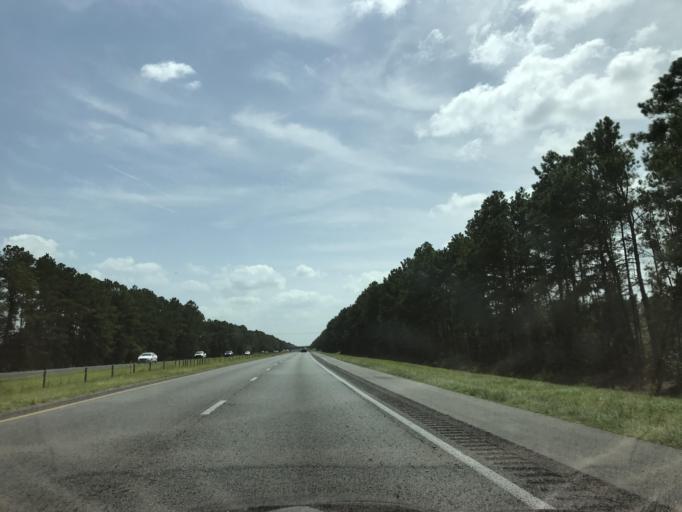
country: US
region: North Carolina
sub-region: Duplin County
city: Wallace
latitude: 34.7422
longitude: -77.9446
